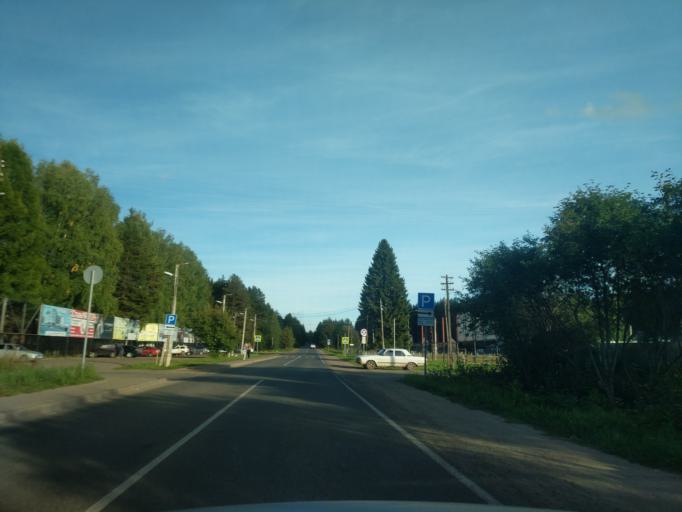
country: RU
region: Kirov
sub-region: Kirovo-Chepetskiy Rayon
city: Kirov
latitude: 58.6070
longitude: 49.8084
